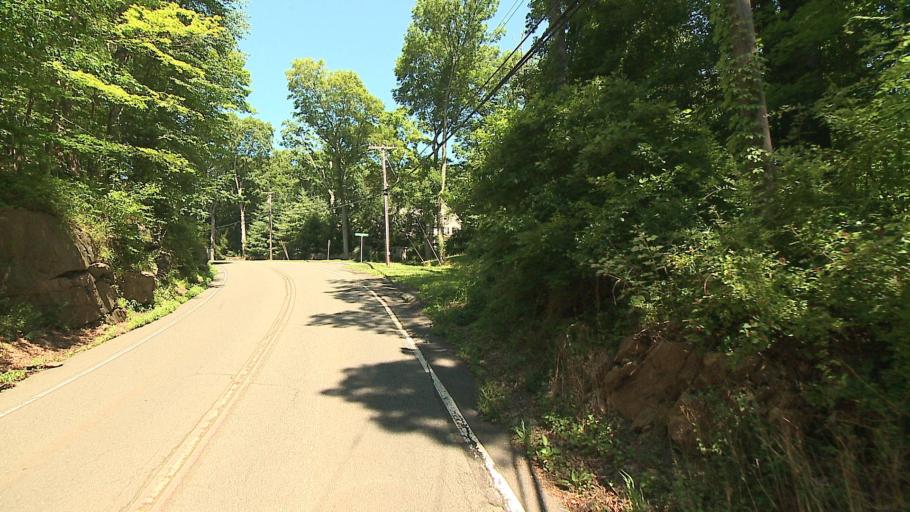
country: US
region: Connecticut
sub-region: Fairfield County
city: Ridgefield
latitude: 41.2943
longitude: -73.5280
